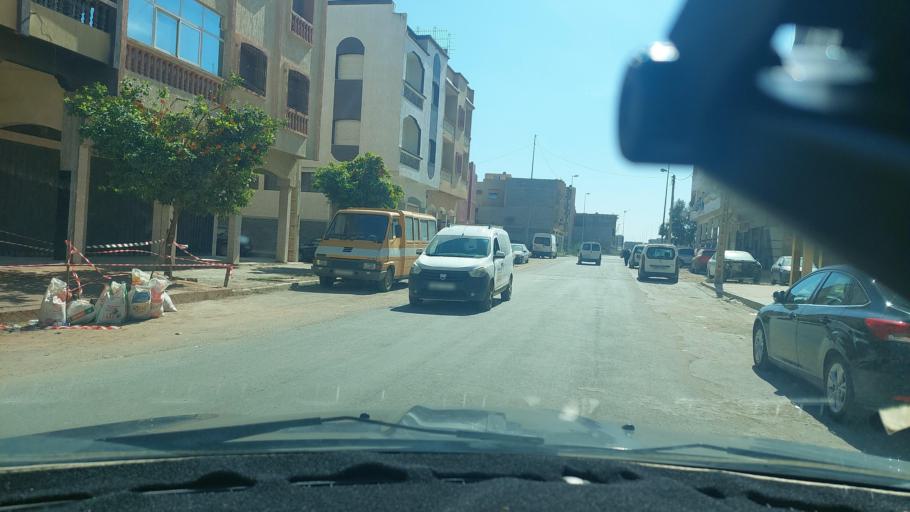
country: MA
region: Grand Casablanca
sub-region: Mediouna
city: Mediouna
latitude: 33.3825
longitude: -7.5365
